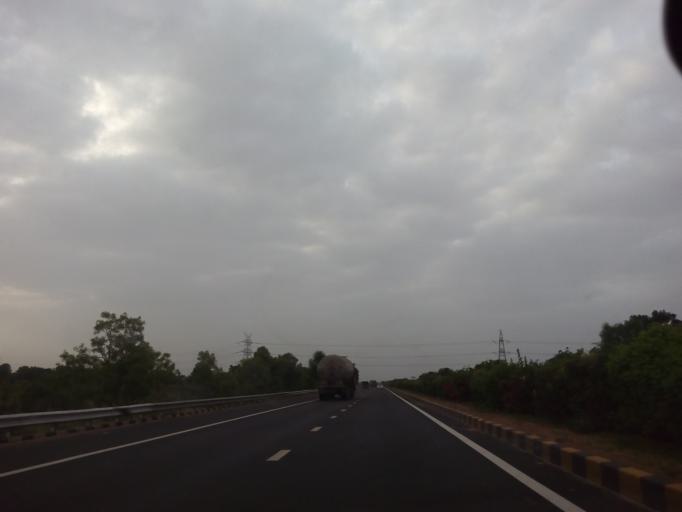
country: IN
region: Gujarat
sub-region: Kheda
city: Mahemdavad
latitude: 22.9362
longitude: 72.7218
